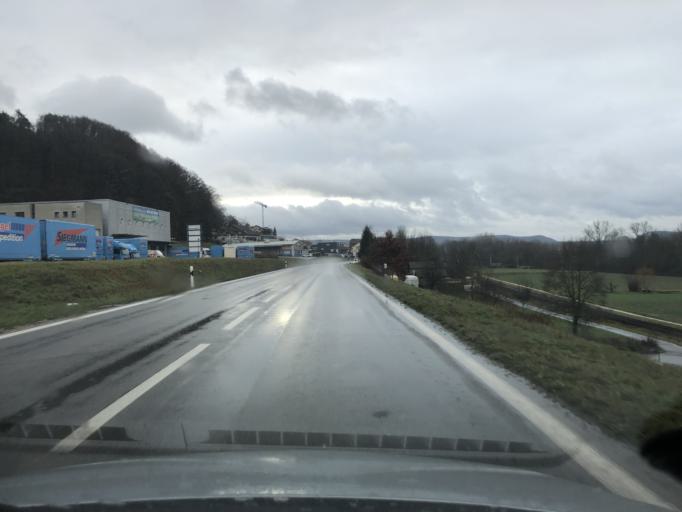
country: CH
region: Aargau
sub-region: Bezirk Zurzach
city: Klingnau
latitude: 47.5916
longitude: 8.2399
